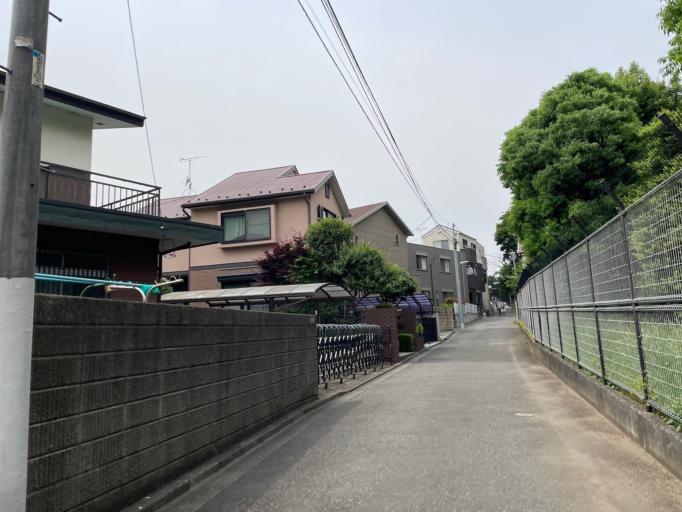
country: JP
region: Tokyo
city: Chofugaoka
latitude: 35.6688
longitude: 139.5451
